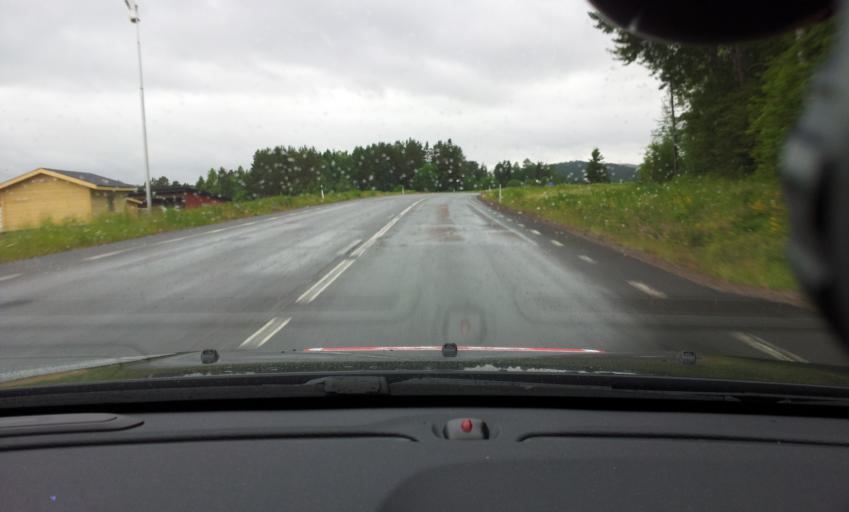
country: SE
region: Jaemtland
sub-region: Ragunda Kommun
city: Hammarstrand
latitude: 63.0358
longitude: 16.5598
